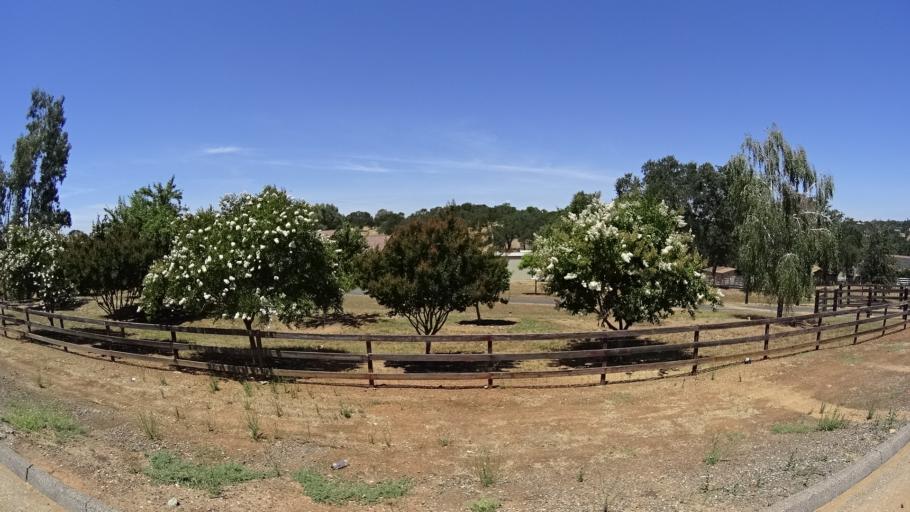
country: US
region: California
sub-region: Calaveras County
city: Rancho Calaveras
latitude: 38.1278
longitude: -120.8449
